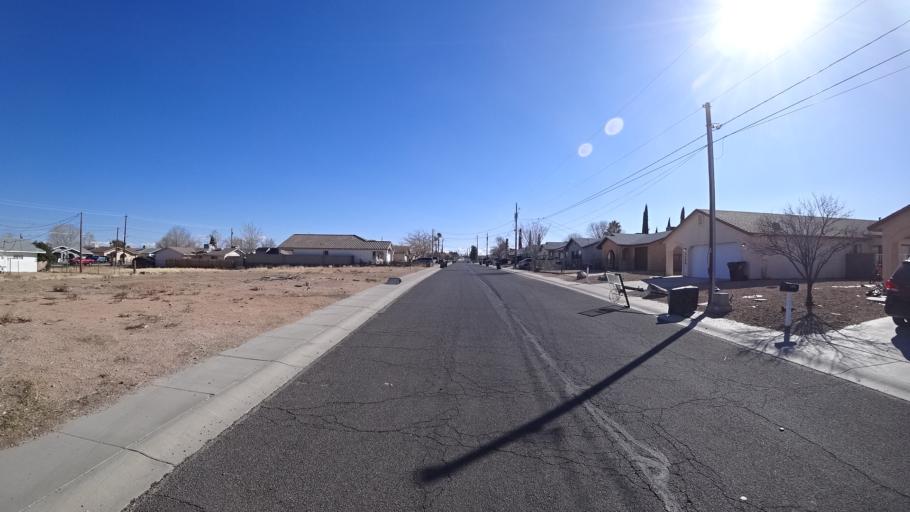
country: US
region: Arizona
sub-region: Mohave County
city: Kingman
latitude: 35.1986
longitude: -114.0157
